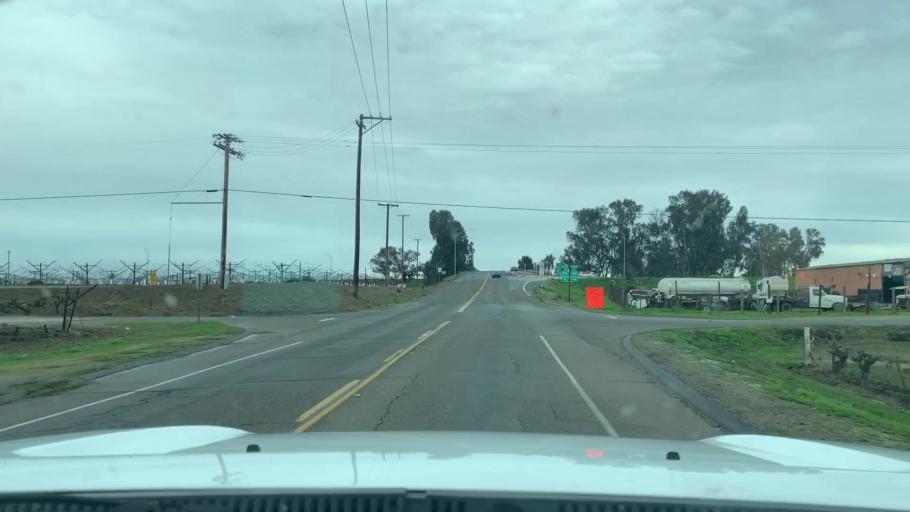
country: US
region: California
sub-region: Fresno County
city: Fowler
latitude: 36.6054
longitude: -119.6647
